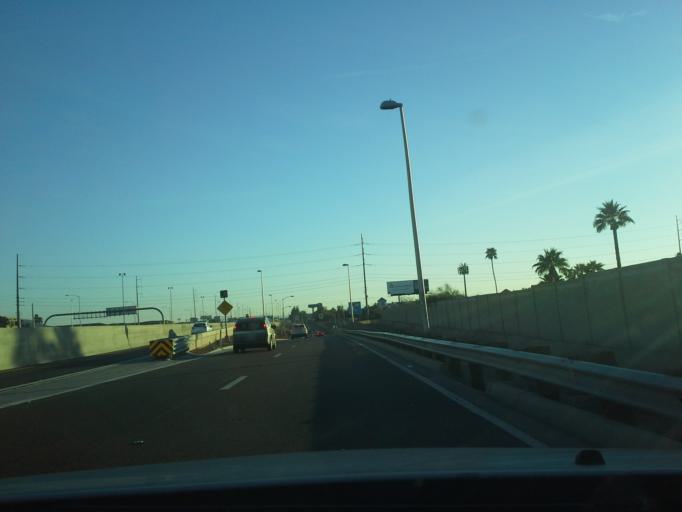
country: US
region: Arizona
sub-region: Maricopa County
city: Glendale
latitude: 33.6572
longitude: -112.1147
